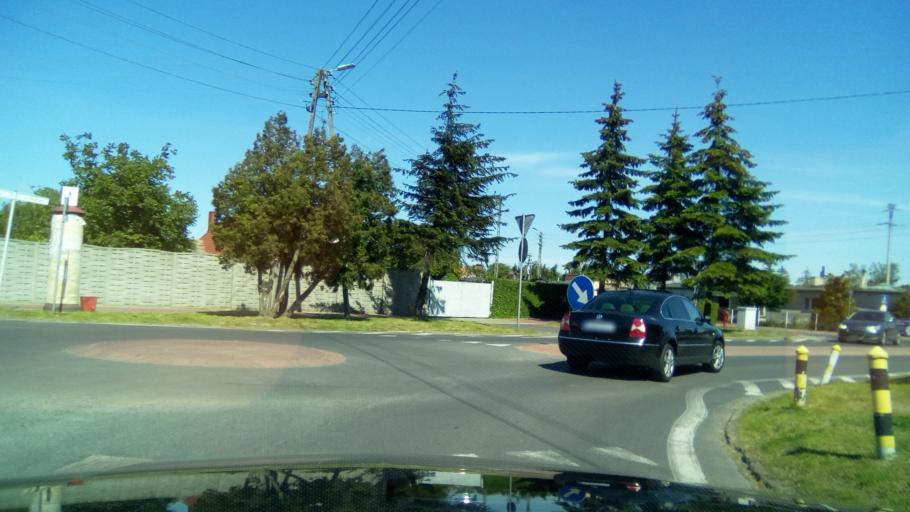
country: PL
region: Greater Poland Voivodeship
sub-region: Powiat gnieznienski
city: Niechanowo
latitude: 52.4648
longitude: 17.6769
